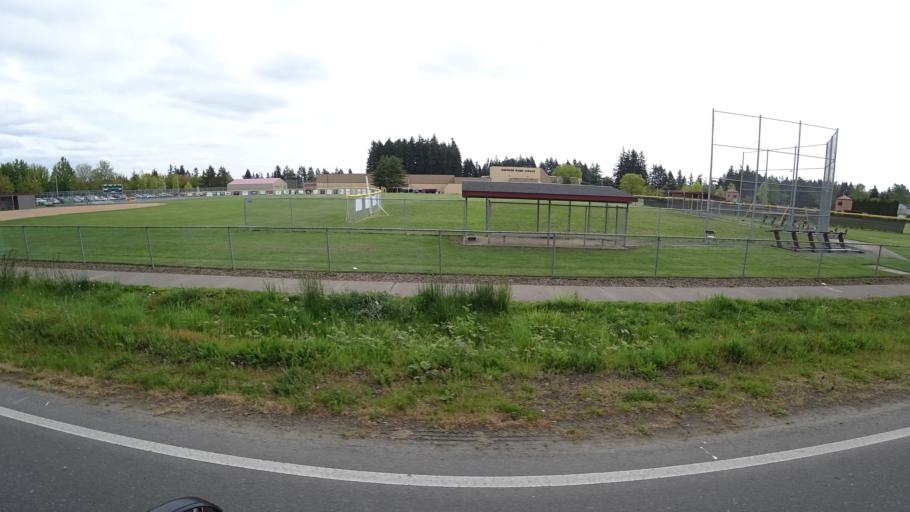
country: US
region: Oregon
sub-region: Washington County
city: Hillsboro
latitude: 45.5419
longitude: -122.9957
